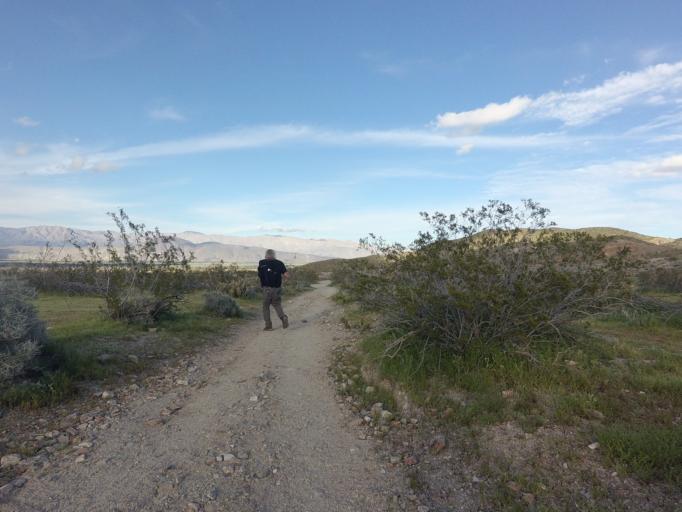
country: US
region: California
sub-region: San Diego County
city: Borrego Springs
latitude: 33.2468
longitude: -116.4082
